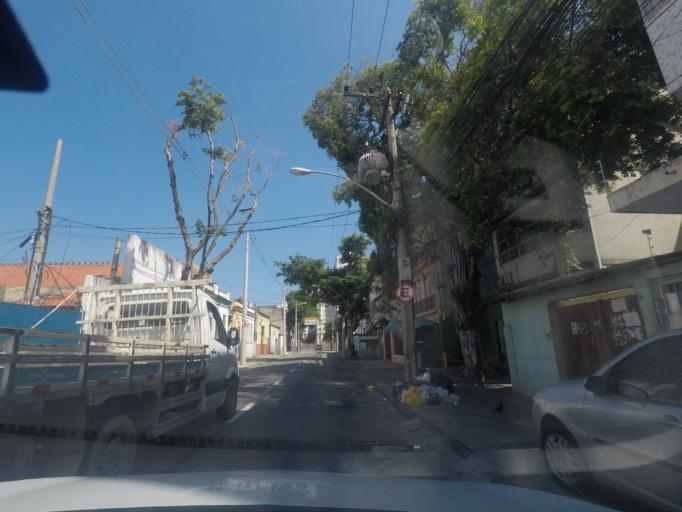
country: BR
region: Rio de Janeiro
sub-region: Rio De Janeiro
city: Rio de Janeiro
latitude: -22.8908
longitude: -43.2212
